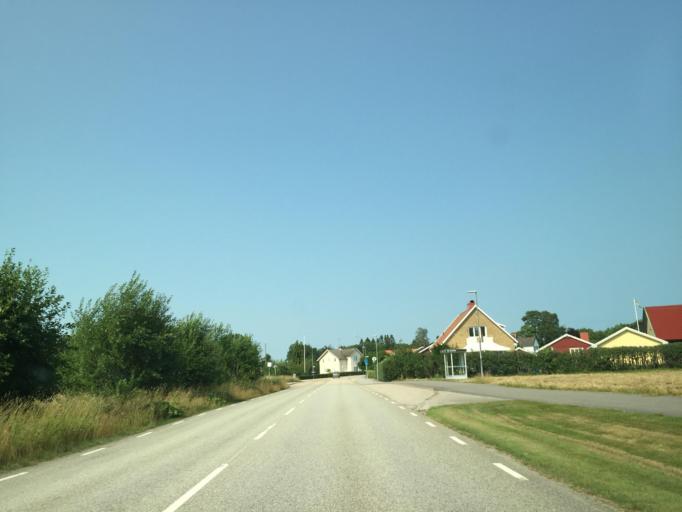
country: SE
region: Vaestra Goetaland
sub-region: Vanersborgs Kommun
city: Vanersborg
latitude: 58.3622
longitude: 12.2762
